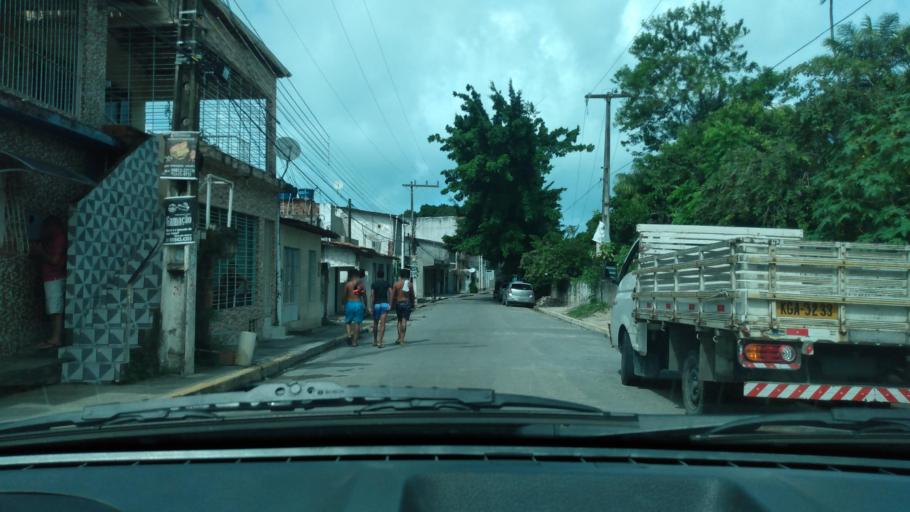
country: BR
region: Pernambuco
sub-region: Cabo De Santo Agostinho
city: Cabo
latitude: -8.3521
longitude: -34.9577
